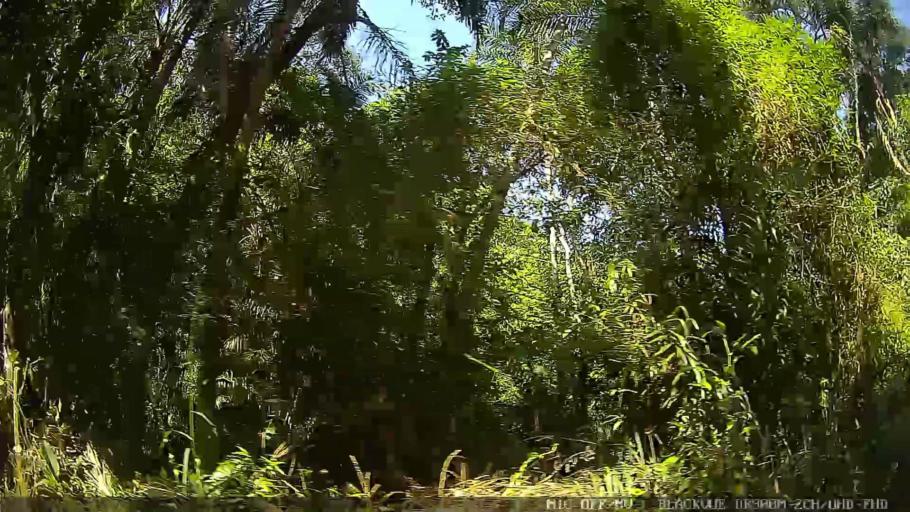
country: BR
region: Sao Paulo
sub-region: Santos
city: Santos
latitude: -24.0027
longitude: -46.3089
